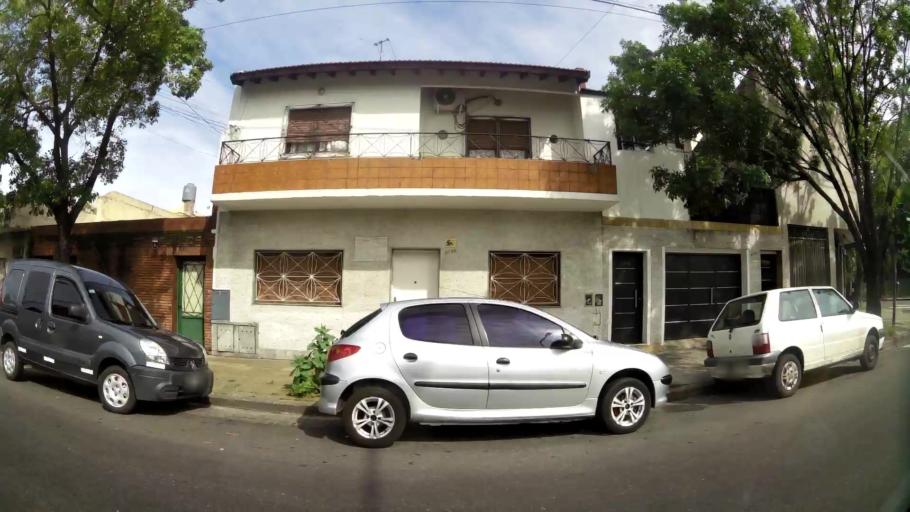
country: AR
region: Buenos Aires F.D.
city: Villa Lugano
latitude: -34.6617
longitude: -58.5051
